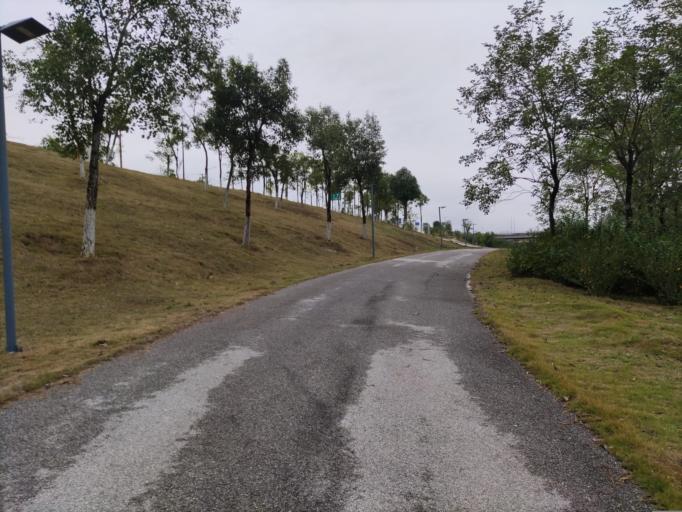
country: CN
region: Guangxi Zhuangzu Zizhiqu
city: Tianzhou
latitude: 23.7817
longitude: 106.7317
